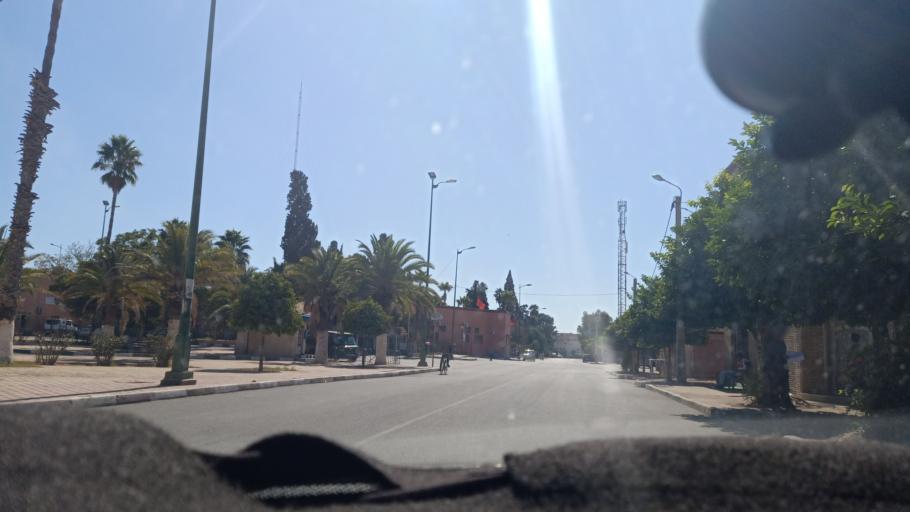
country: MA
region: Doukkala-Abda
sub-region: Safi
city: Youssoufia
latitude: 32.2450
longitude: -8.5332
